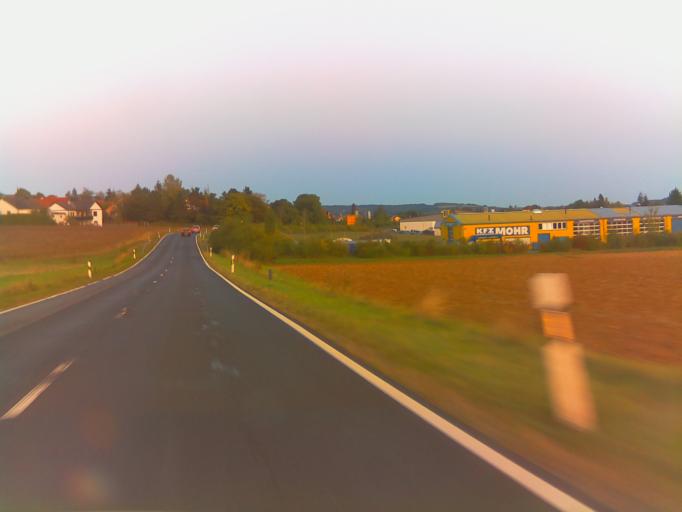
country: DE
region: Bavaria
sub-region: Regierungsbezirk Unterfranken
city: Oerlenbach
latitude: 50.1480
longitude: 10.1244
